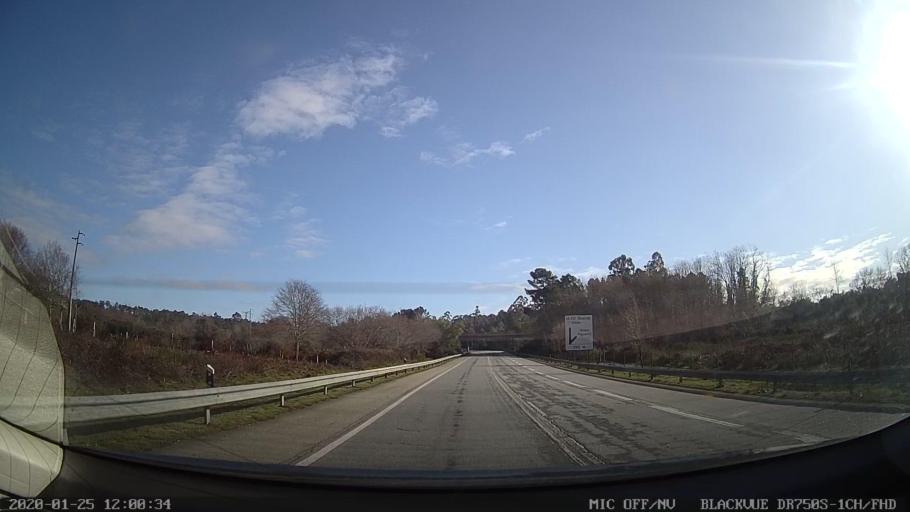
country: PT
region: Viseu
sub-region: Viseu
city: Abraveses
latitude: 40.6660
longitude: -8.0009
